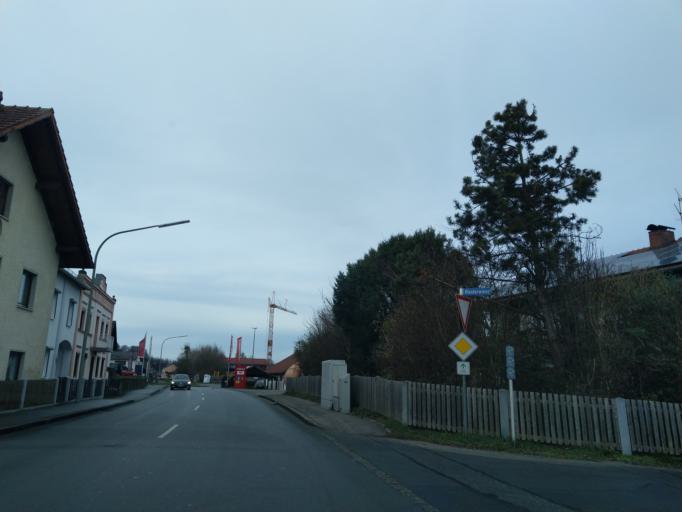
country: DE
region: Bavaria
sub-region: Lower Bavaria
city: Osterhofen
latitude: 48.6933
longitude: 13.0208
